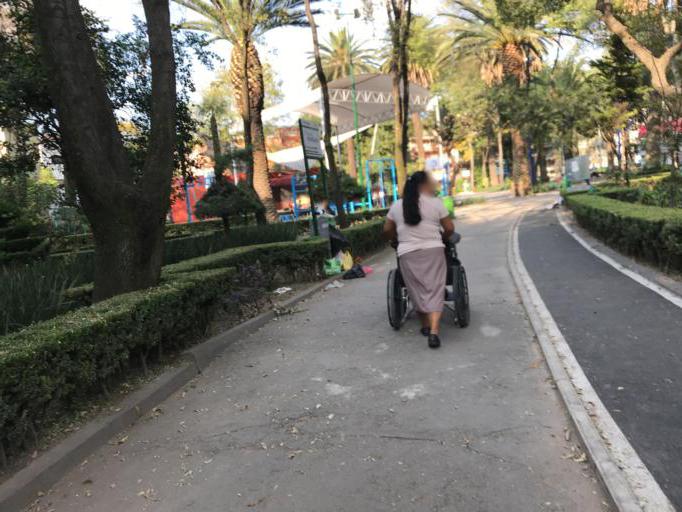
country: MX
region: Mexico City
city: Benito Juarez
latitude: 19.4006
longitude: -99.1488
